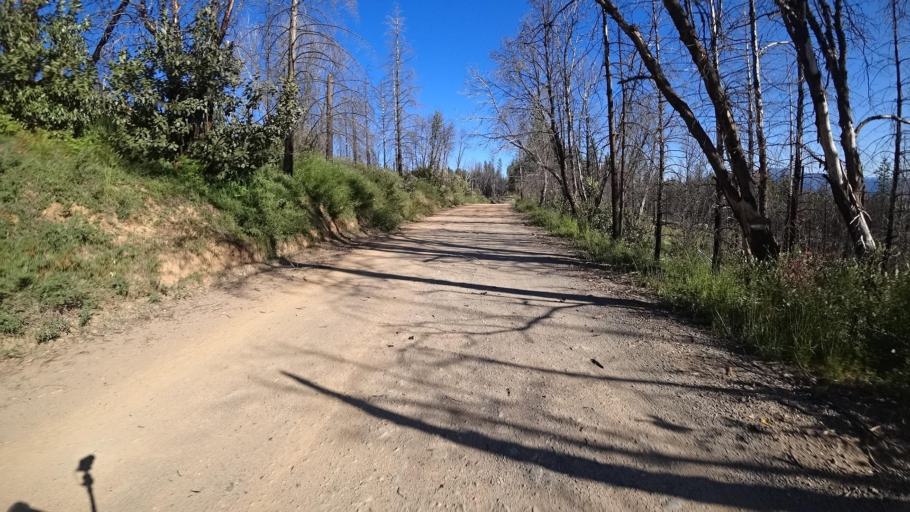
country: US
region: California
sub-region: Lake County
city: Upper Lake
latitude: 39.3428
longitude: -122.9610
